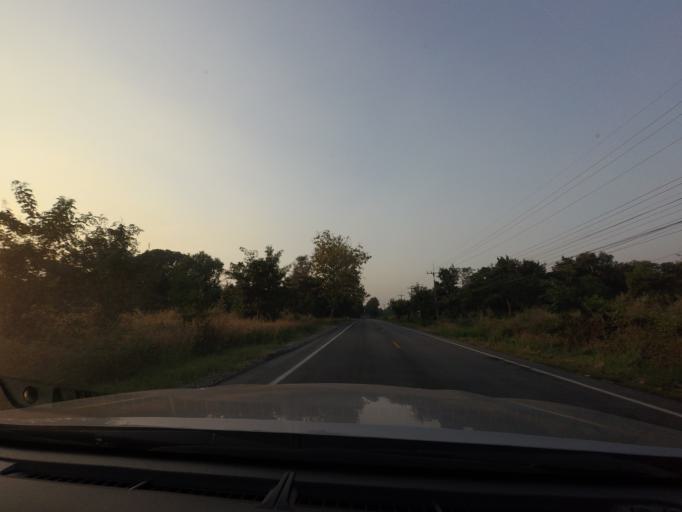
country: TH
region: Phitsanulok
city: Wang Thong
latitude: 16.7294
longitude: 100.4572
